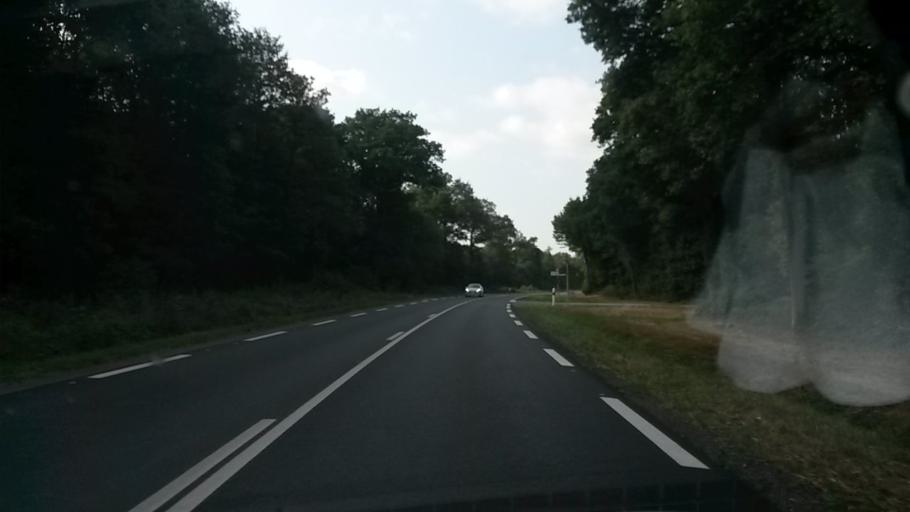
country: FR
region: Haute-Normandie
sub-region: Departement de l'Eure
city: Tillieres-sur-Avre
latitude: 48.7965
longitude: 0.9933
